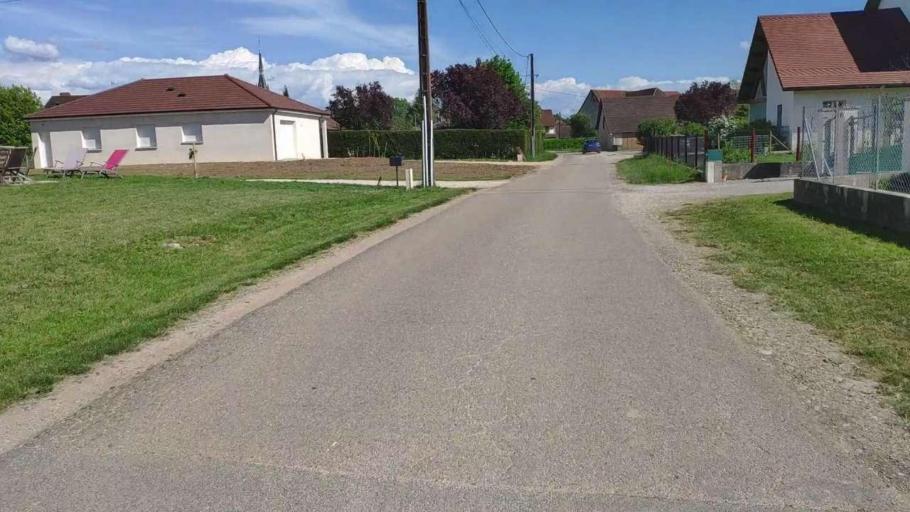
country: FR
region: Franche-Comte
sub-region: Departement du Jura
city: Bletterans
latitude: 46.7654
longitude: 5.4711
